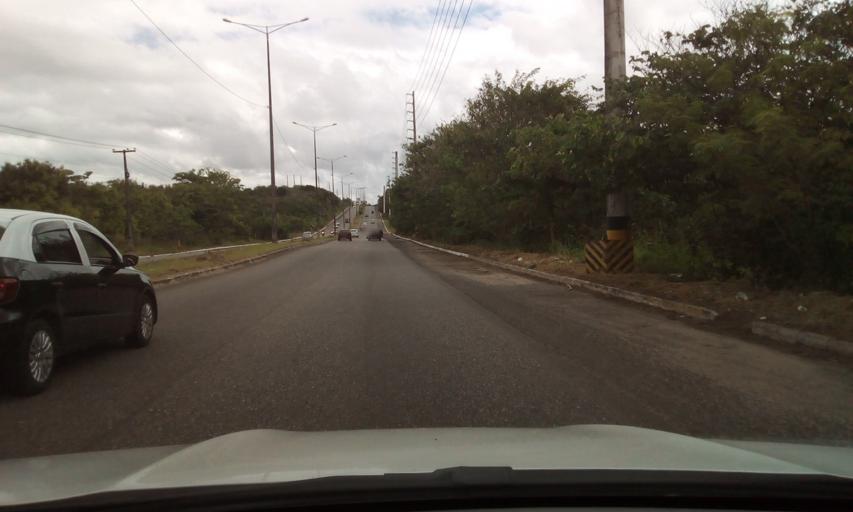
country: BR
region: Paraiba
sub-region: Bayeux
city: Bayeux
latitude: -7.1351
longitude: -34.9053
